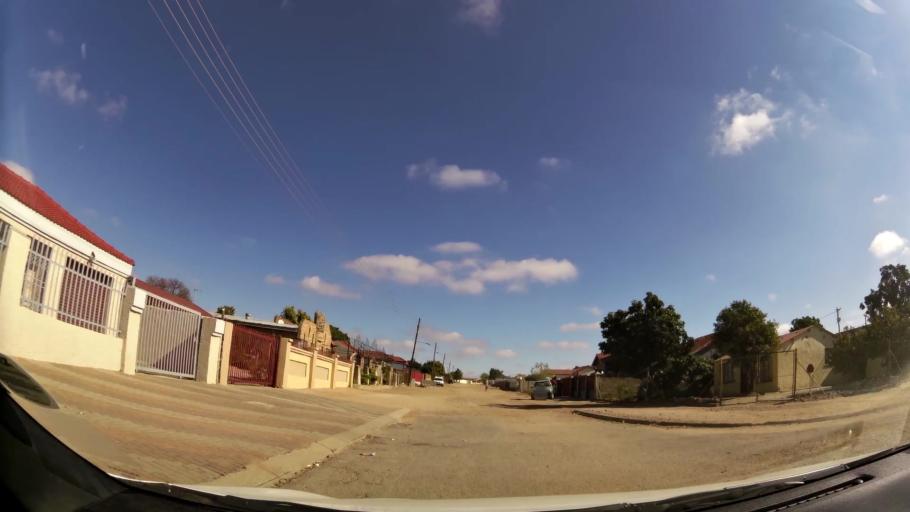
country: ZA
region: Limpopo
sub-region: Capricorn District Municipality
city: Polokwane
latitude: -23.8670
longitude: 29.3891
